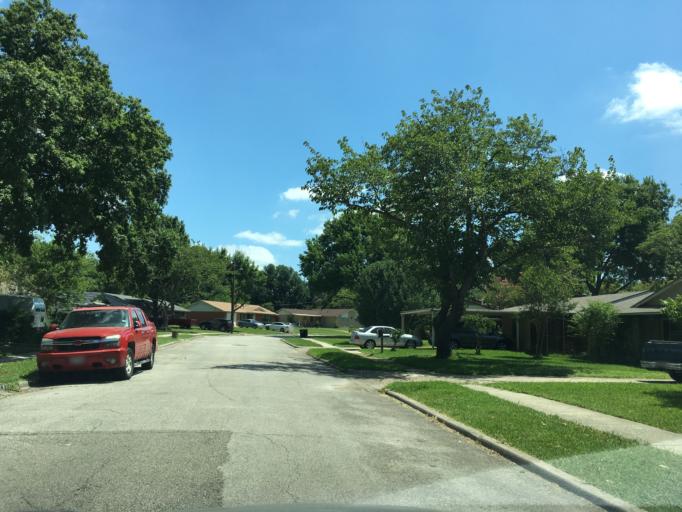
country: US
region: Texas
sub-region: Dallas County
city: Garland
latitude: 32.8354
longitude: -96.6519
